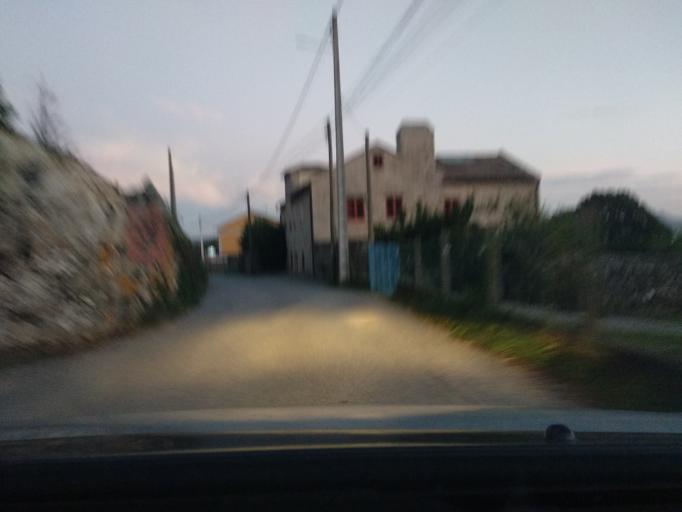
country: ES
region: Galicia
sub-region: Provincia de Pontevedra
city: Moana
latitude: 42.2864
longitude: -8.7505
